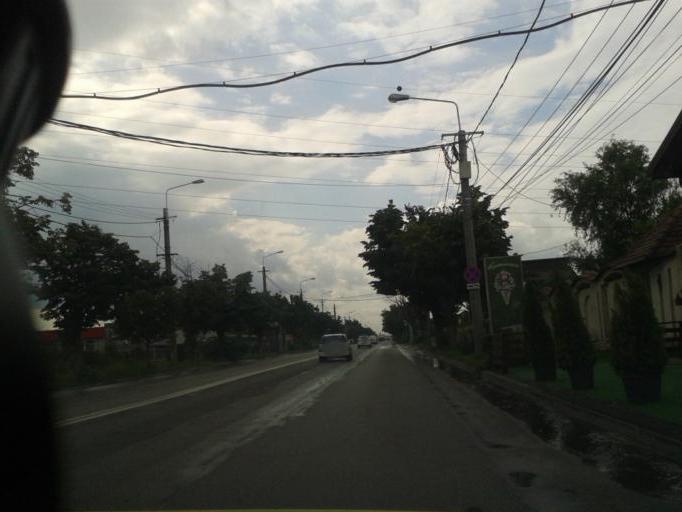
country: RO
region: Prahova
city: Ploiesti
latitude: 44.9610
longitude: 25.9792
